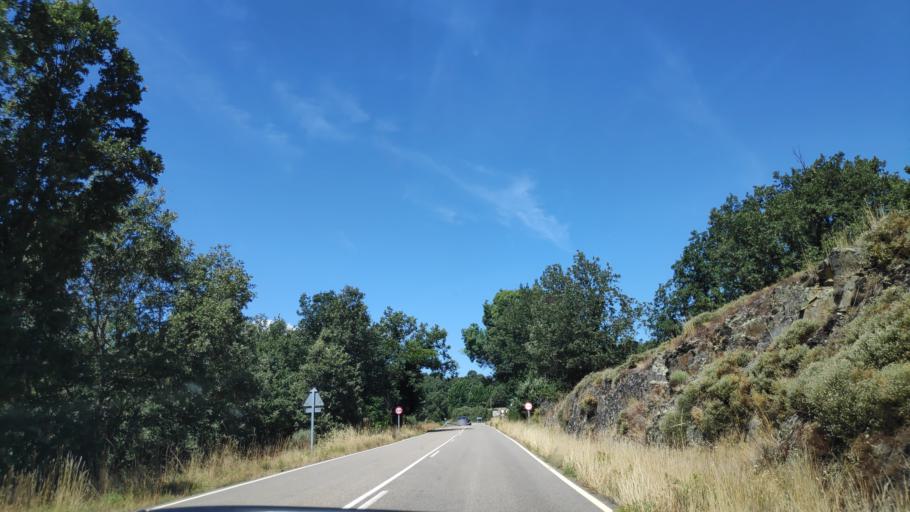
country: ES
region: Castille and Leon
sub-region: Provincia de Zamora
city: Puebla de Sanabria
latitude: 42.0595
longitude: -6.6452
